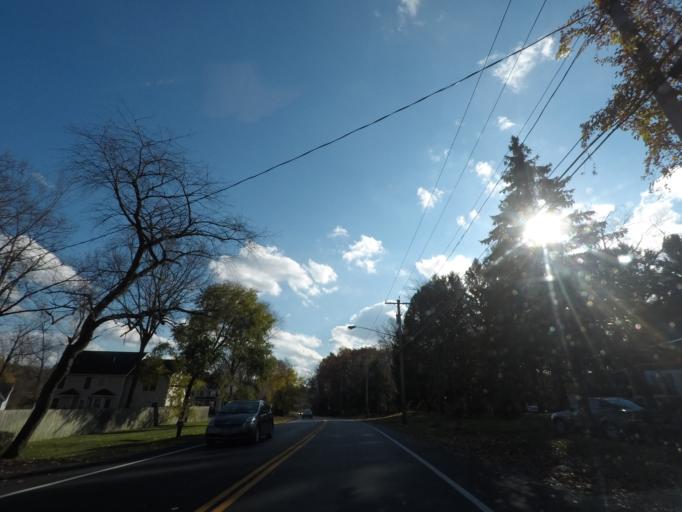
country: US
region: New York
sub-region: Schenectady County
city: Niskayuna
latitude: 42.7917
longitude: -73.8936
